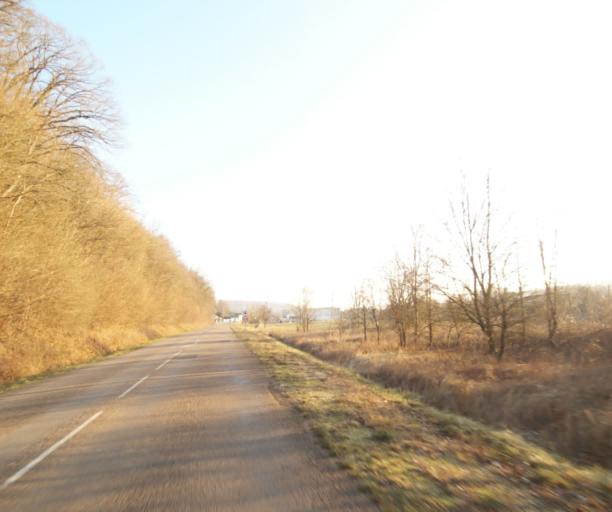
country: FR
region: Champagne-Ardenne
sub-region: Departement de la Haute-Marne
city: Chevillon
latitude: 48.5280
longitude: 5.1097
